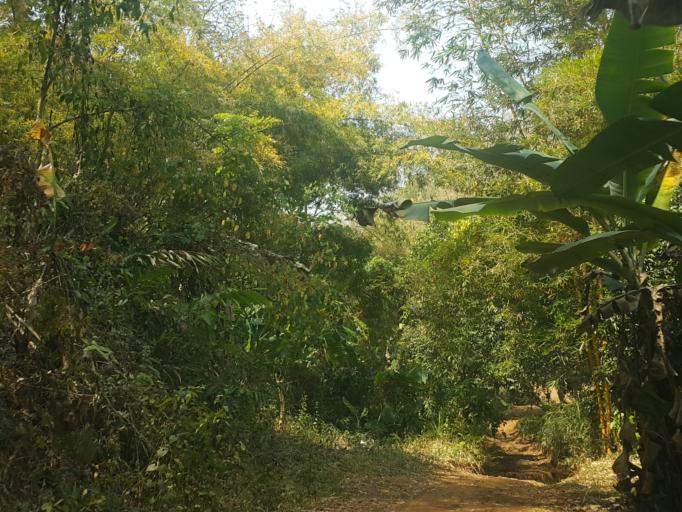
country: TH
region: Chiang Mai
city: Hang Dong
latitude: 18.7575
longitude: 98.8226
